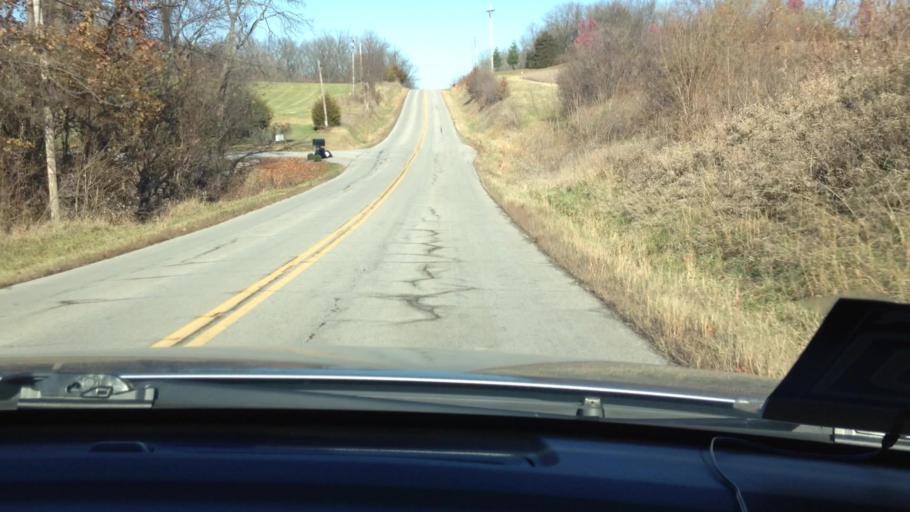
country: US
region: Missouri
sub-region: Platte County
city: Weston
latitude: 39.4584
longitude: -94.9007
